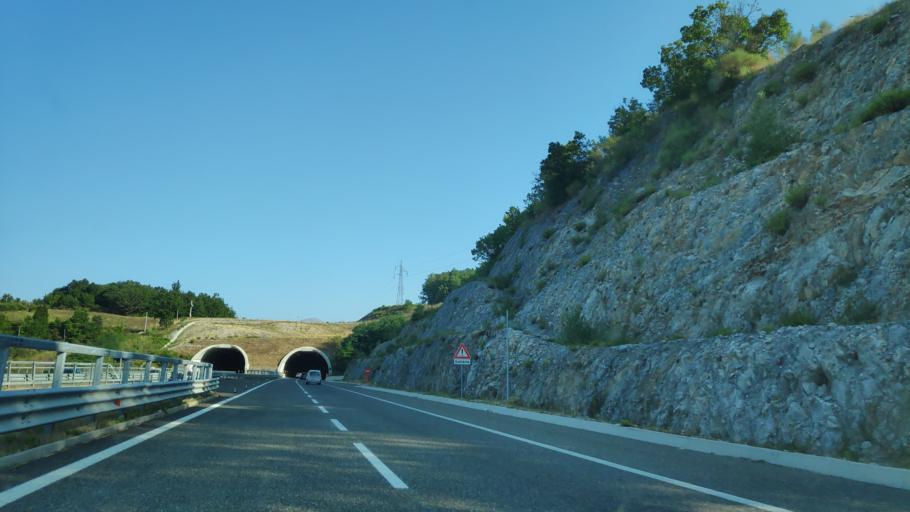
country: IT
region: Basilicate
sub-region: Provincia di Potenza
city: Lauria
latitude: 40.0273
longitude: 15.8765
